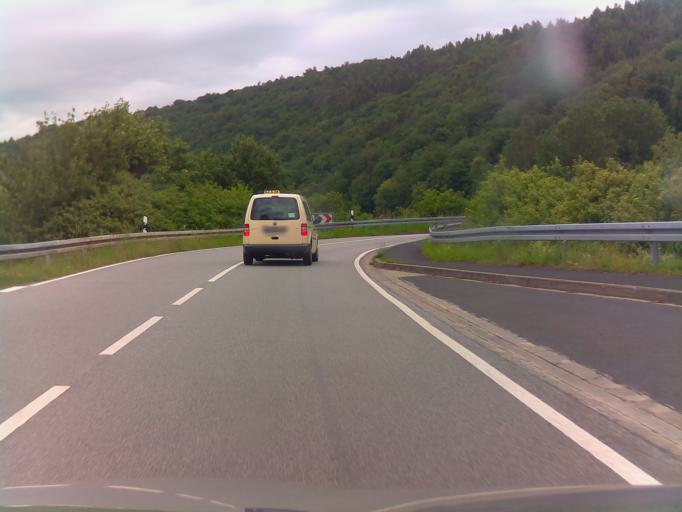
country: DE
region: Bavaria
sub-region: Regierungsbezirk Unterfranken
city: Grafendorf
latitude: 50.1082
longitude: 9.7243
